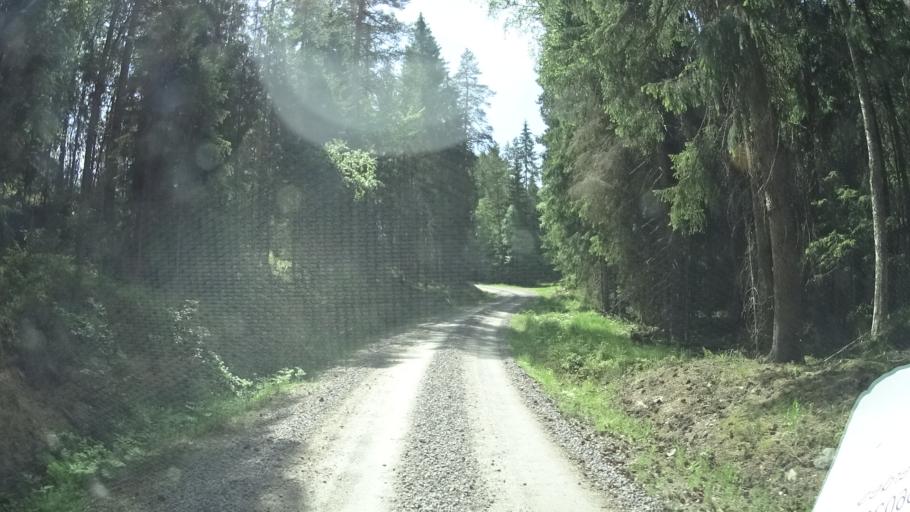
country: SE
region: OEstergoetland
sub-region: Norrkopings Kommun
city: Svartinge
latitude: 58.7743
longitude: 15.9297
